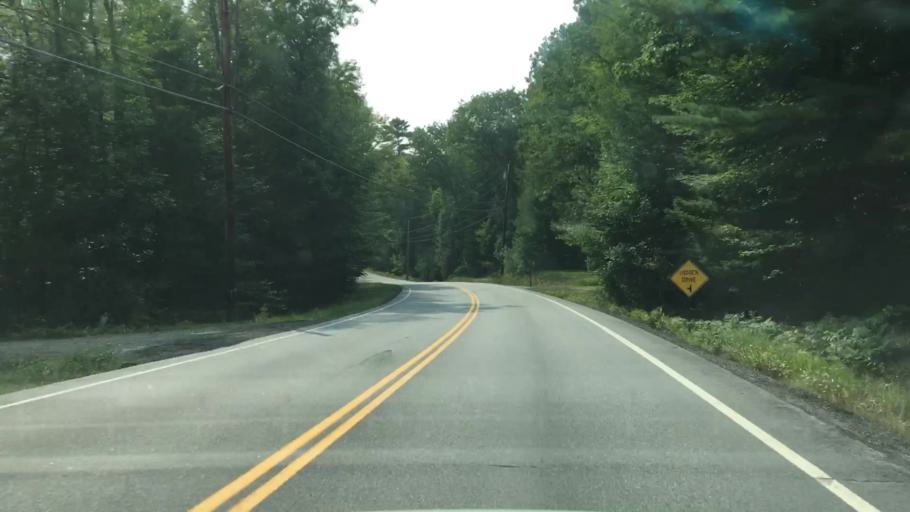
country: US
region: Maine
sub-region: Oxford County
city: Paris
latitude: 44.2364
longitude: -70.4800
